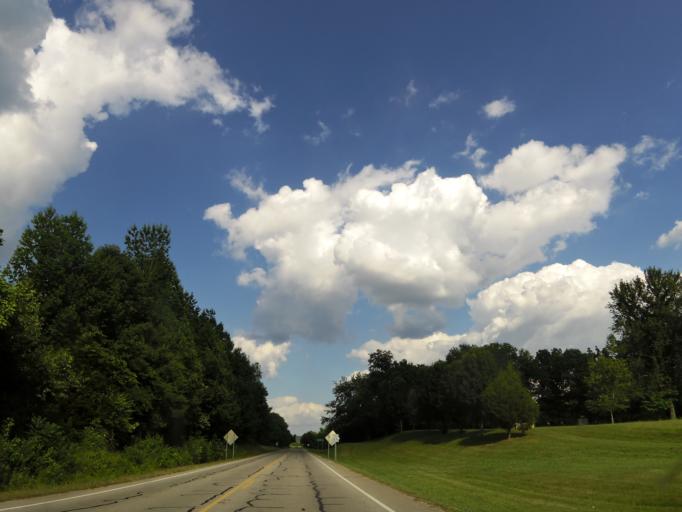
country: US
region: Tennessee
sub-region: Perry County
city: Linden
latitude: 35.6363
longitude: -87.7873
